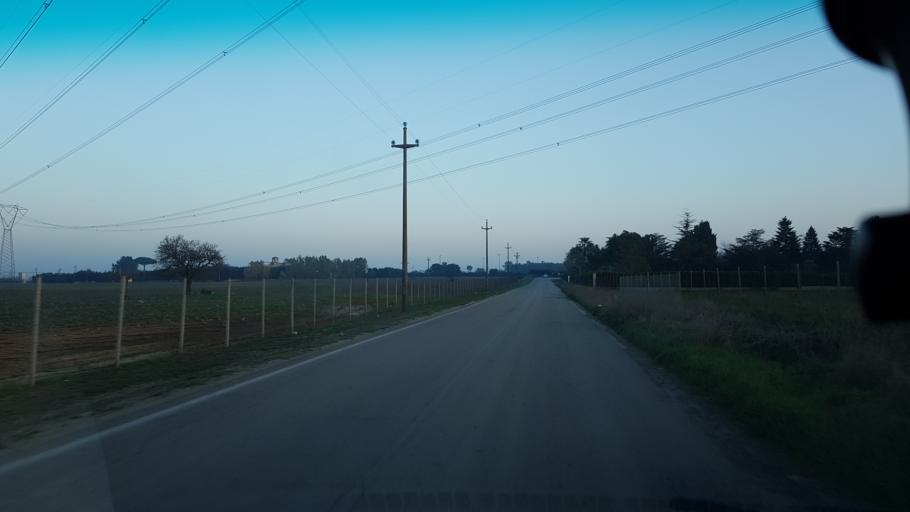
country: IT
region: Apulia
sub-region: Provincia di Brindisi
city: Mesagne
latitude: 40.5836
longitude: 17.8005
